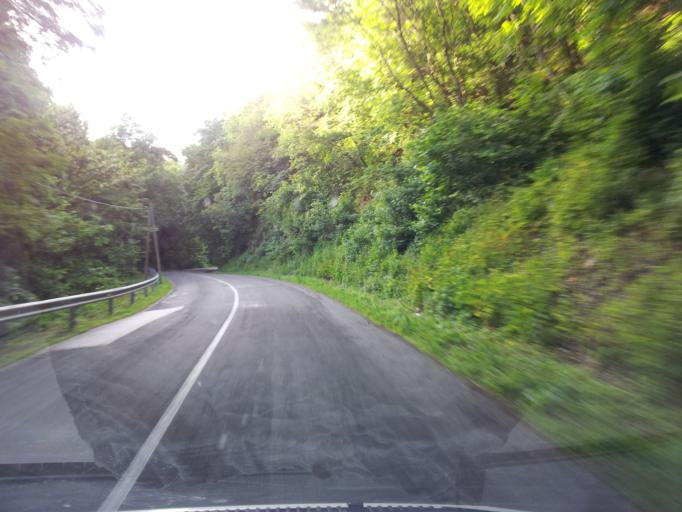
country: HU
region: Komarom-Esztergom
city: Kesztolc
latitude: 47.7411
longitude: 18.8083
